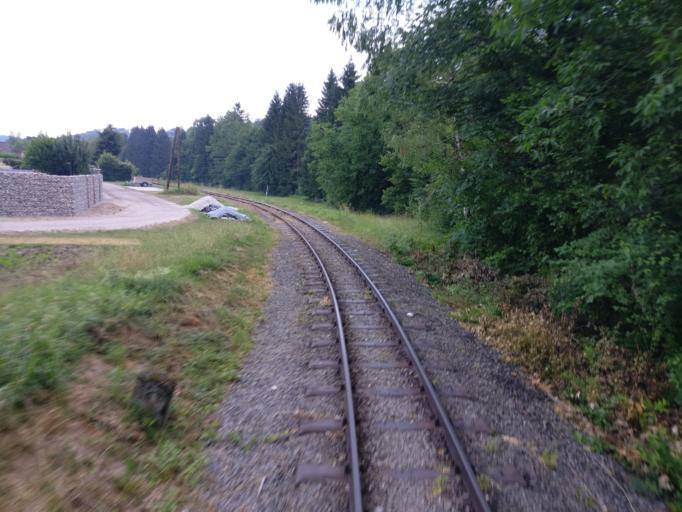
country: AT
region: Upper Austria
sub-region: Politischer Bezirk Kirchdorf an der Krems
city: Gruenburg
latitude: 47.9825
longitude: 14.2756
